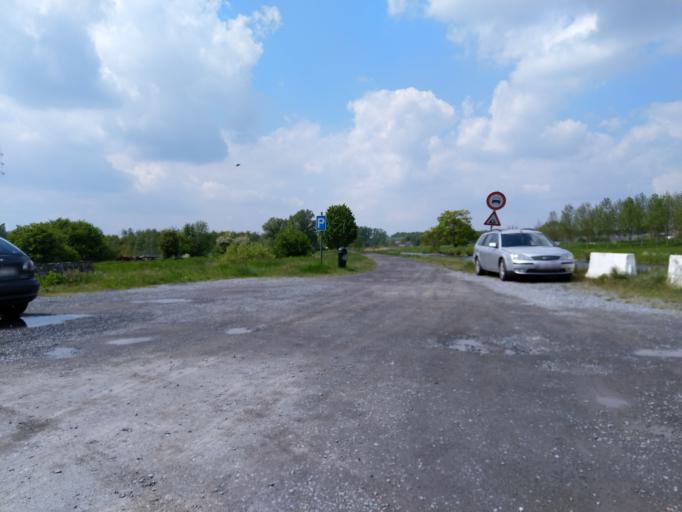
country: BE
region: Wallonia
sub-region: Province du Hainaut
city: Roeulx
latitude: 50.4727
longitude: 4.0640
